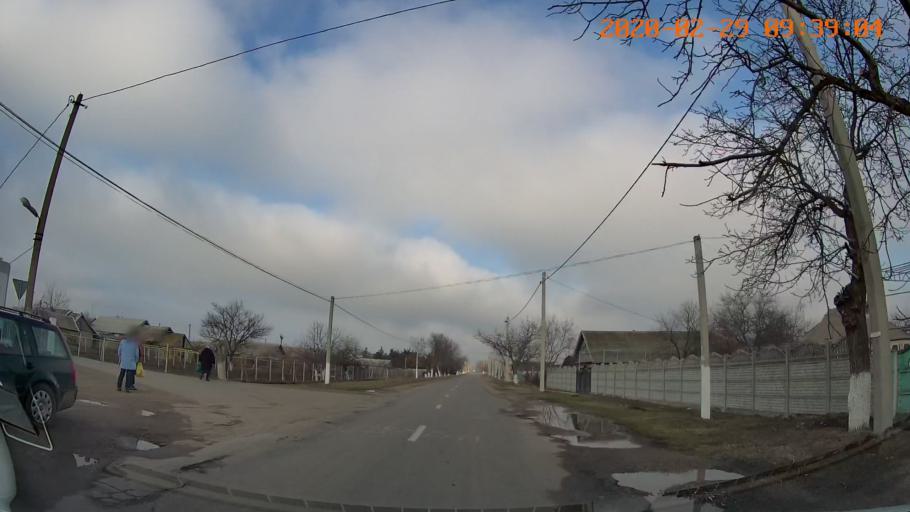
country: MD
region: Telenesti
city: Crasnoe
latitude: 46.6338
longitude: 29.8590
